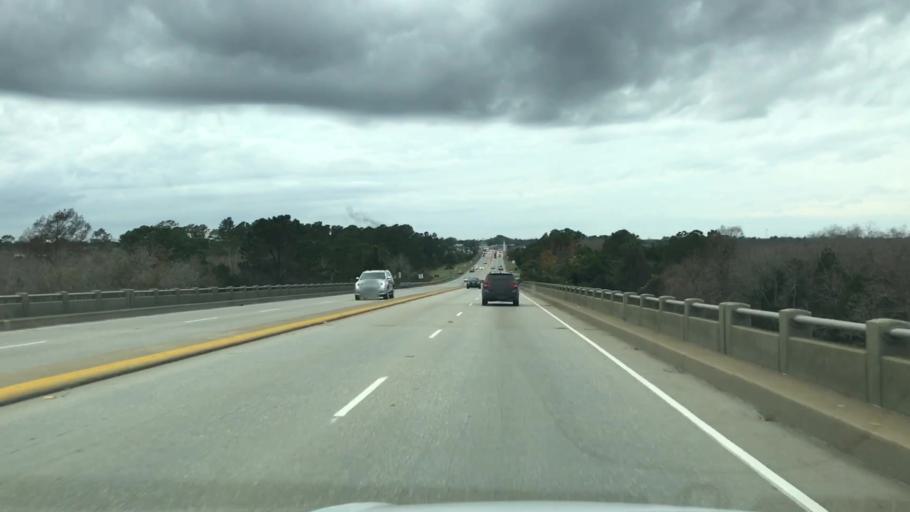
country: US
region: South Carolina
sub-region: Georgetown County
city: Georgetown
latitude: 33.3661
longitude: -79.2566
